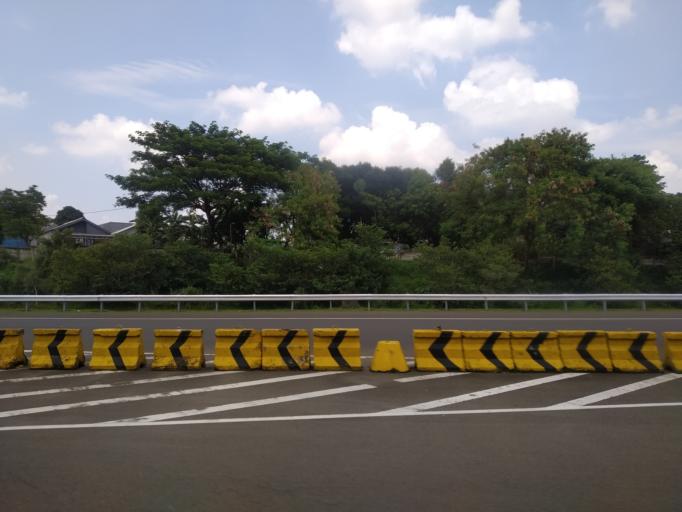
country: ID
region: West Java
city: Bogor
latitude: -6.5987
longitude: 106.8154
